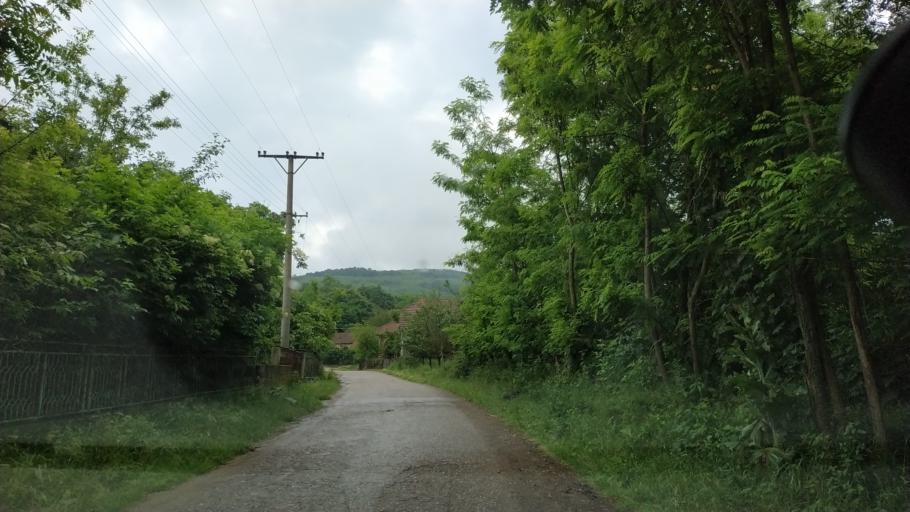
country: RS
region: Central Serbia
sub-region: Nisavski Okrug
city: Aleksinac
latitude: 43.4308
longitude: 21.6506
